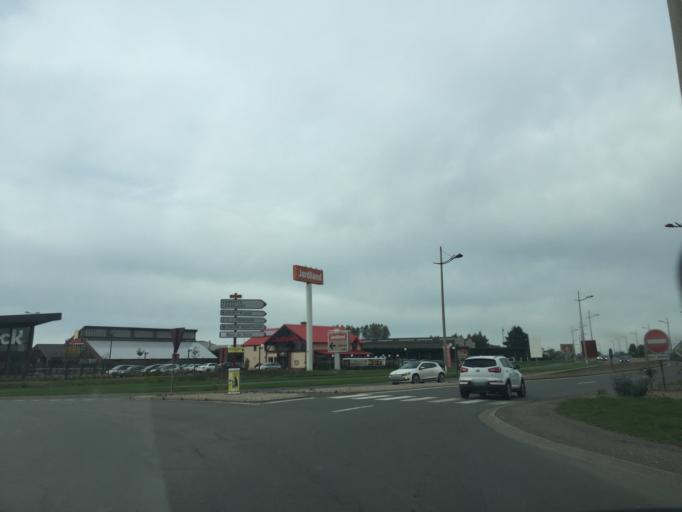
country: FR
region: Nord-Pas-de-Calais
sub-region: Departement du Pas-de-Calais
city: Calais
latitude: 50.9412
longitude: 1.8383
